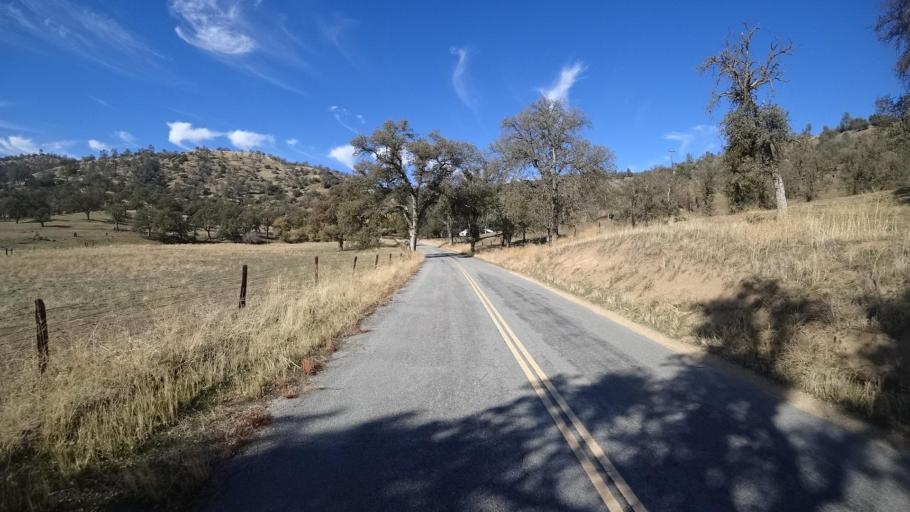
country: US
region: California
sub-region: Kern County
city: Alta Sierra
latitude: 35.6308
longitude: -118.7514
